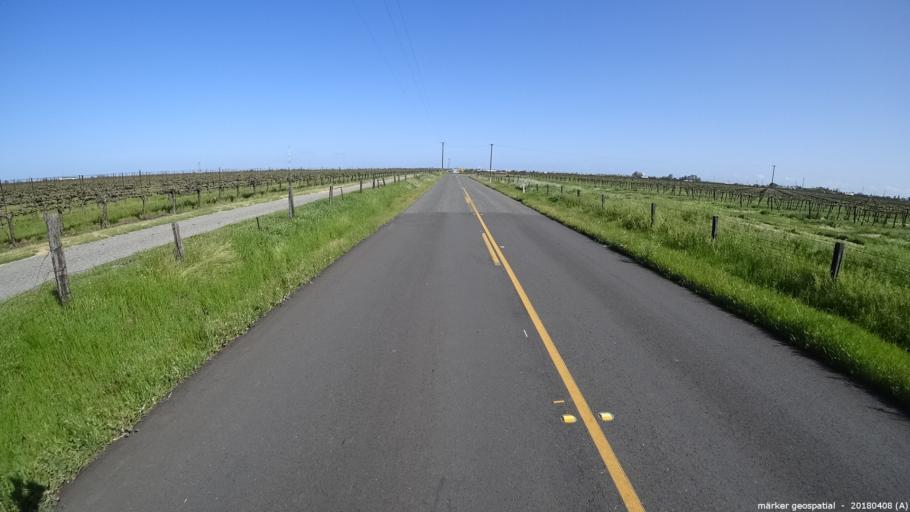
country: US
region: California
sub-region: Sacramento County
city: Elk Grove
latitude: 38.3606
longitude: -121.3713
